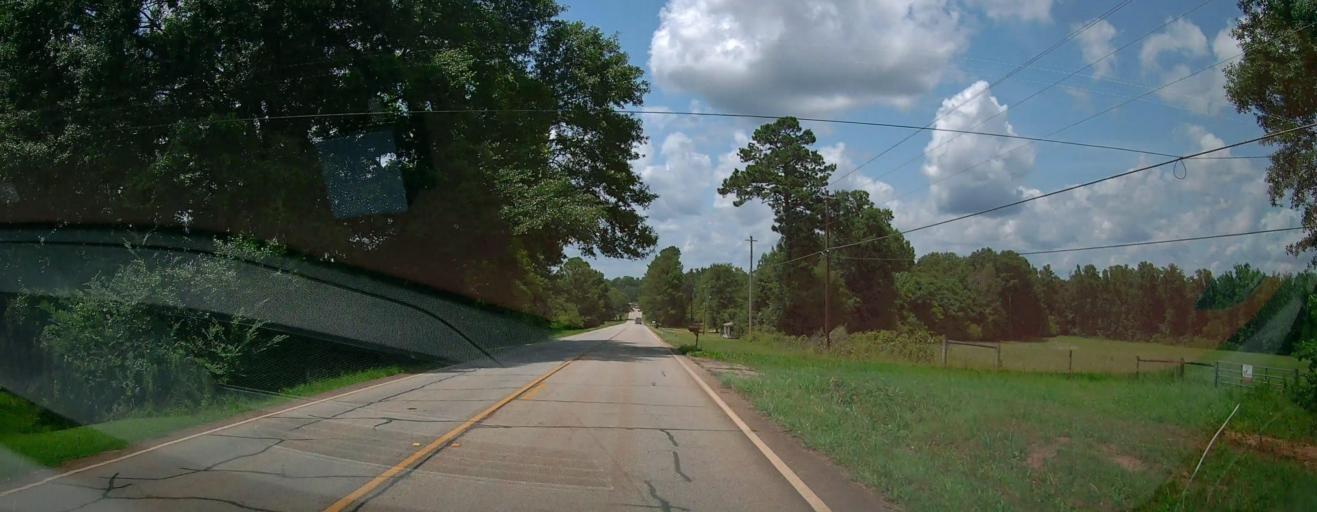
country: US
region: Georgia
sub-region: Troup County
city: Hogansville
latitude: 33.2199
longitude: -84.9288
